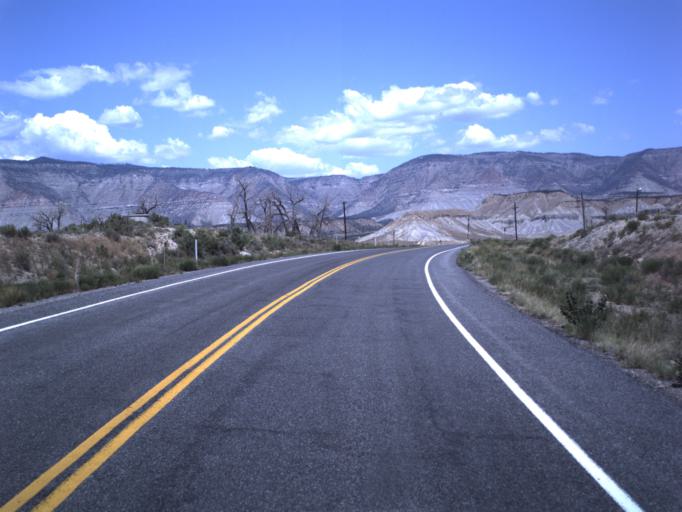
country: US
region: Utah
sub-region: Emery County
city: Orangeville
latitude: 39.2375
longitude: -111.0879
